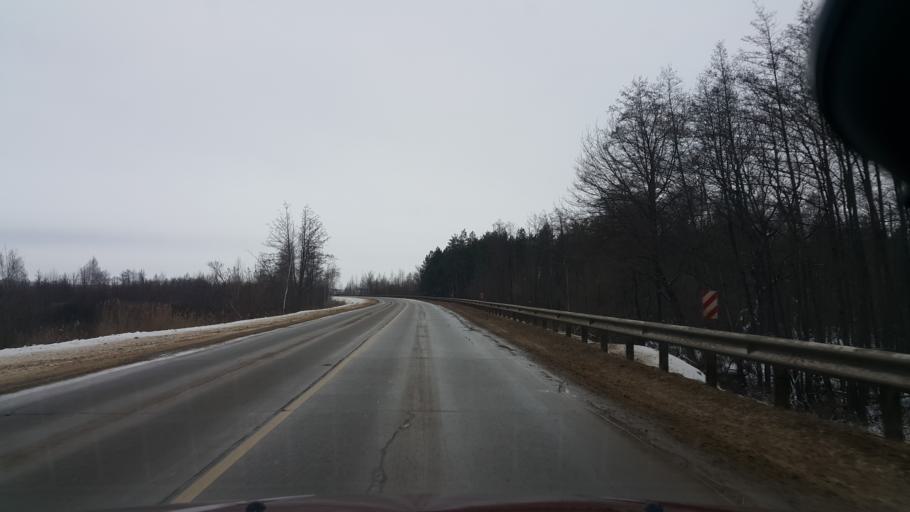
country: RU
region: Tambov
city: Bokino
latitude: 52.6300
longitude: 41.5020
